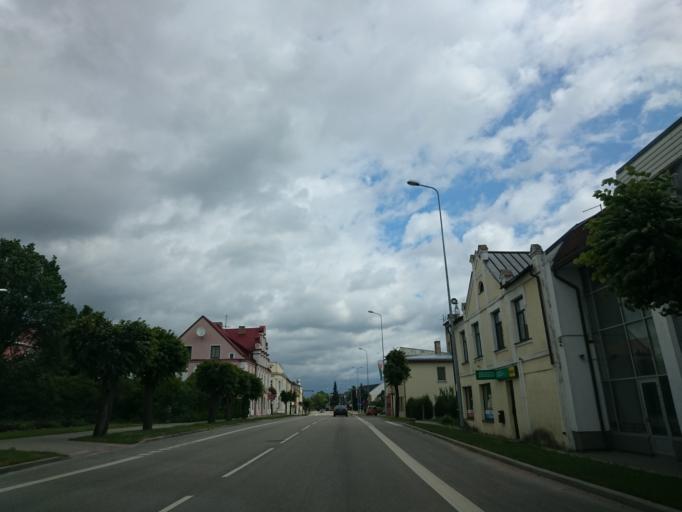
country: LV
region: Madonas Rajons
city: Madona
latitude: 56.8521
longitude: 26.2212
